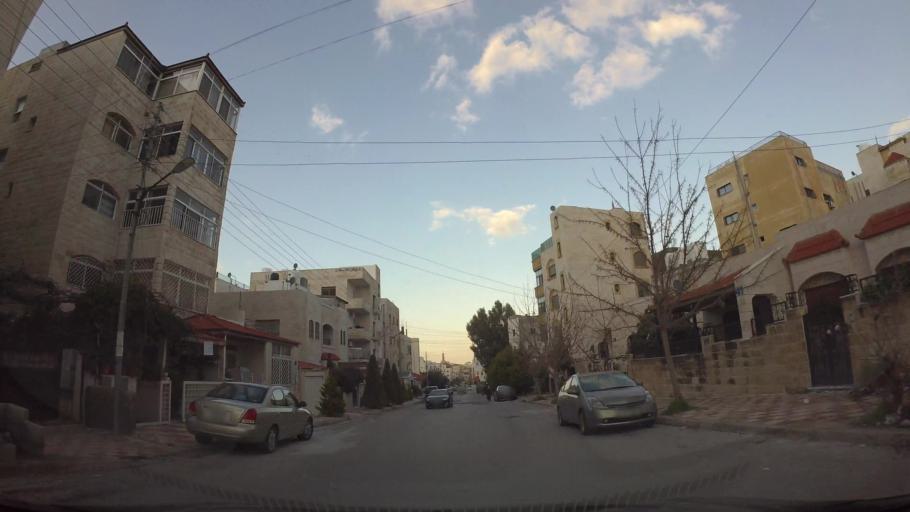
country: JO
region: Amman
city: Al Bunayyat ash Shamaliyah
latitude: 31.9153
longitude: 35.8906
